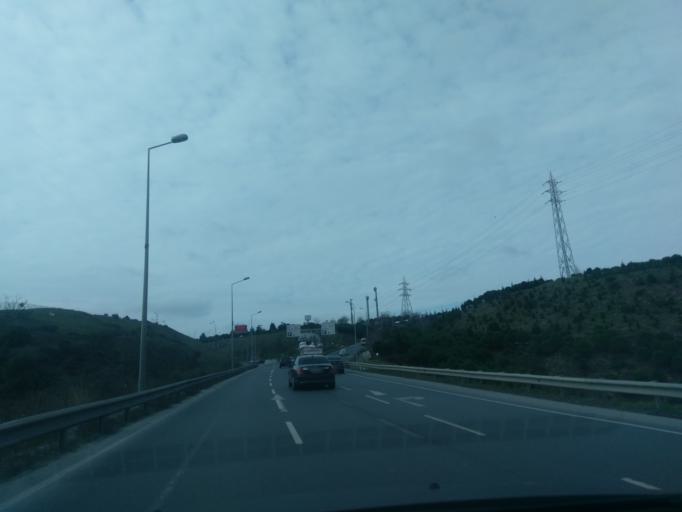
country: TR
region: Istanbul
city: Basaksehir
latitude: 41.0628
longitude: 28.7718
